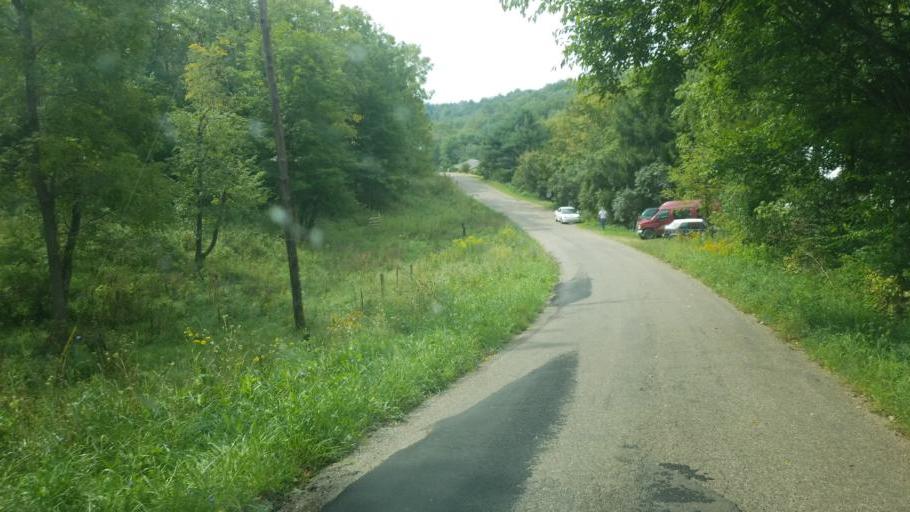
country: US
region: Ohio
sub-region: Knox County
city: Danville
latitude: 40.4861
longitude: -82.3359
